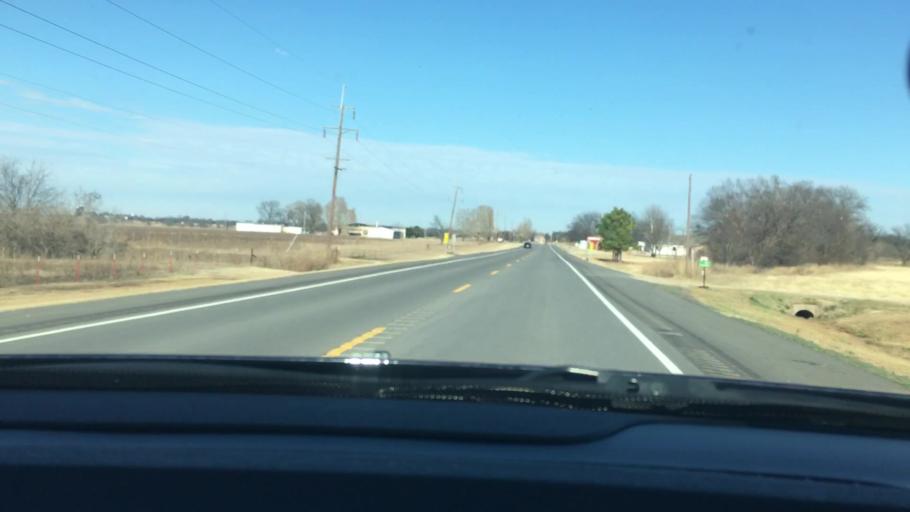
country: US
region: Oklahoma
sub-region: Garvin County
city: Wynnewood
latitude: 34.5893
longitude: -97.1425
